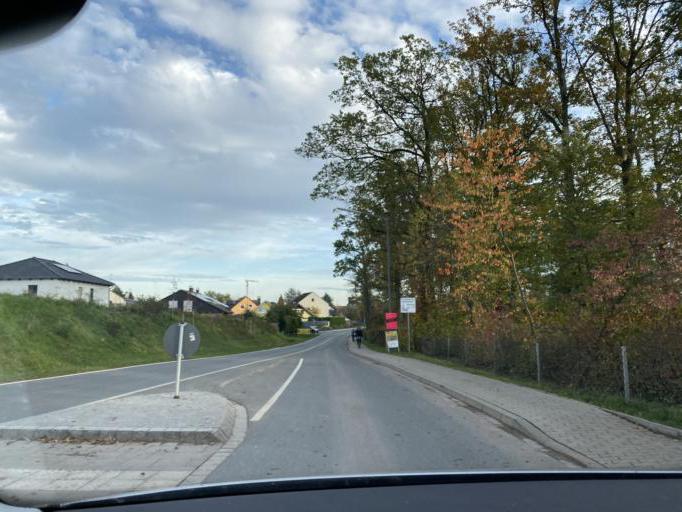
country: DE
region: Bavaria
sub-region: Regierungsbezirk Mittelfranken
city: Puschendorf
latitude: 49.5268
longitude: 10.8230
